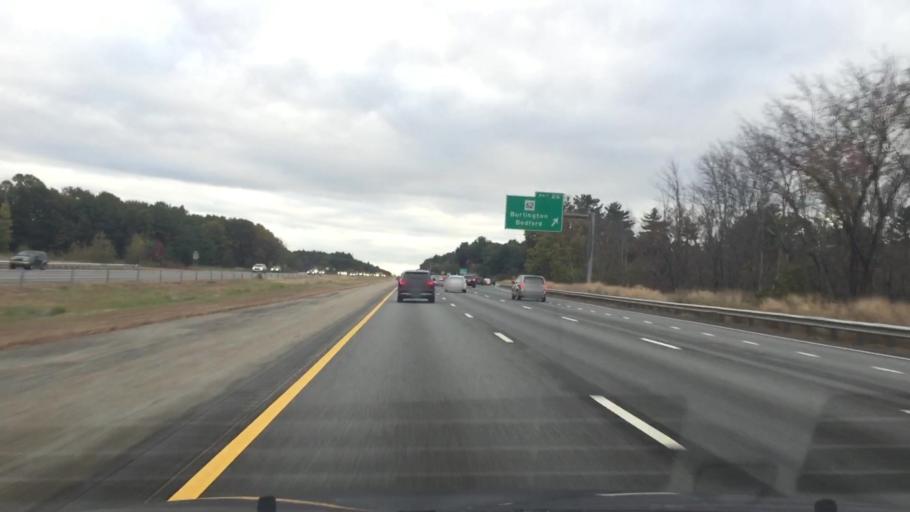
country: US
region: Massachusetts
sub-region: Middlesex County
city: Pinehurst
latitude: 42.5078
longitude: -71.2493
